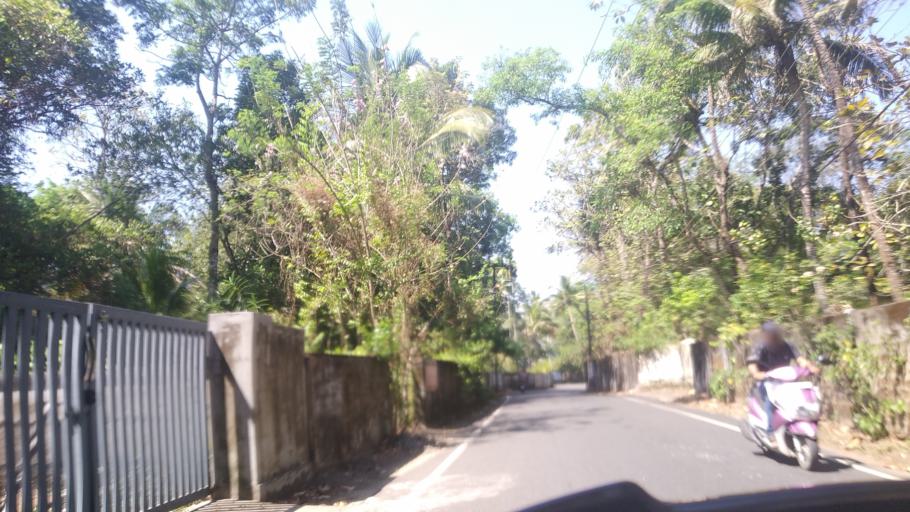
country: IN
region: Kerala
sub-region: Thrissur District
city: Kodungallur
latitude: 10.1370
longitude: 76.2256
